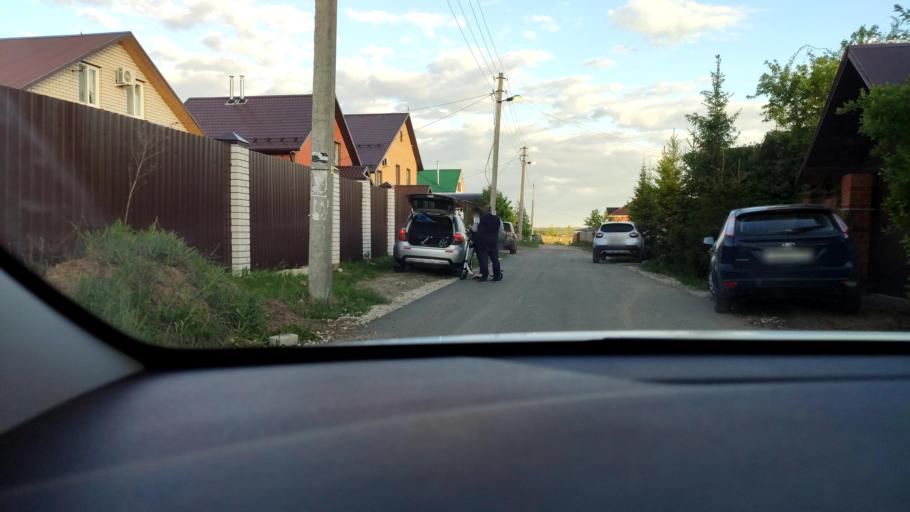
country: RU
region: Tatarstan
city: Stolbishchi
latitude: 55.7661
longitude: 49.2704
